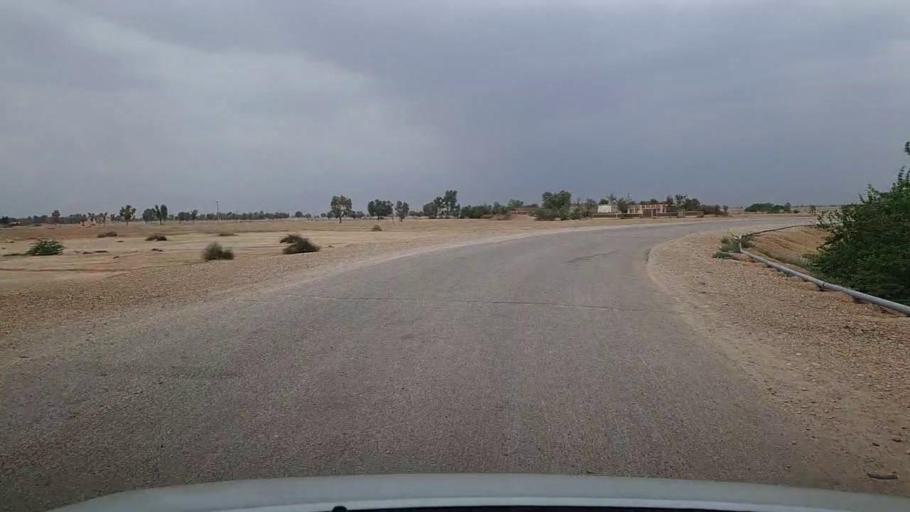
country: PK
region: Sindh
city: Sehwan
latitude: 26.3350
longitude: 67.7275
